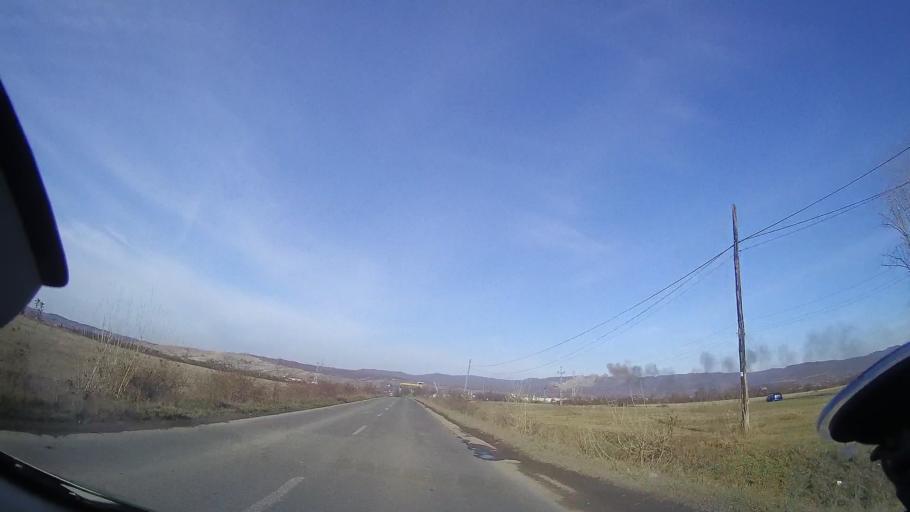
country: RO
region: Bihor
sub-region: Comuna Astileu
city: Astileu
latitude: 47.0392
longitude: 22.3915
